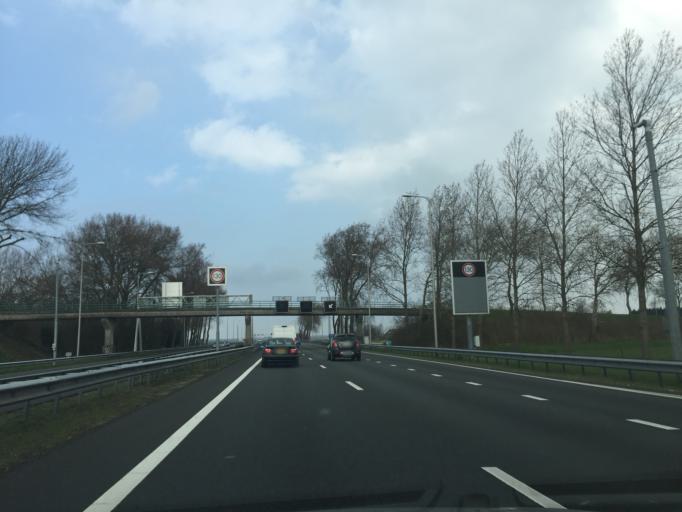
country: NL
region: North Holland
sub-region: Gemeente Uitgeest
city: Uitgeest
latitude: 52.5511
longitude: 4.7194
